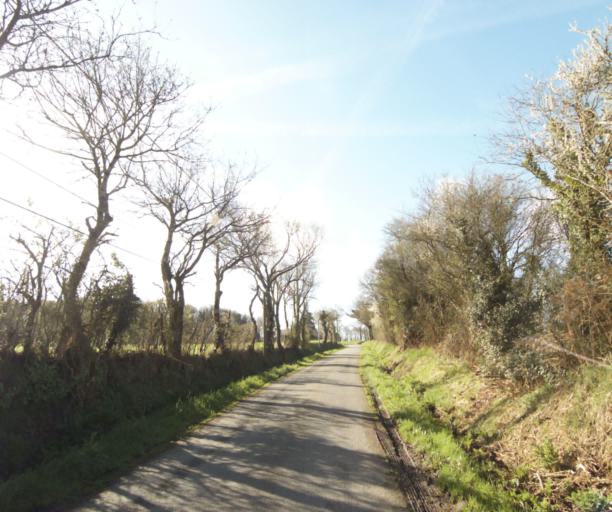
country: FR
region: Pays de la Loire
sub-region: Departement de la Loire-Atlantique
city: Bouvron
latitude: 47.4006
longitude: -1.8480
